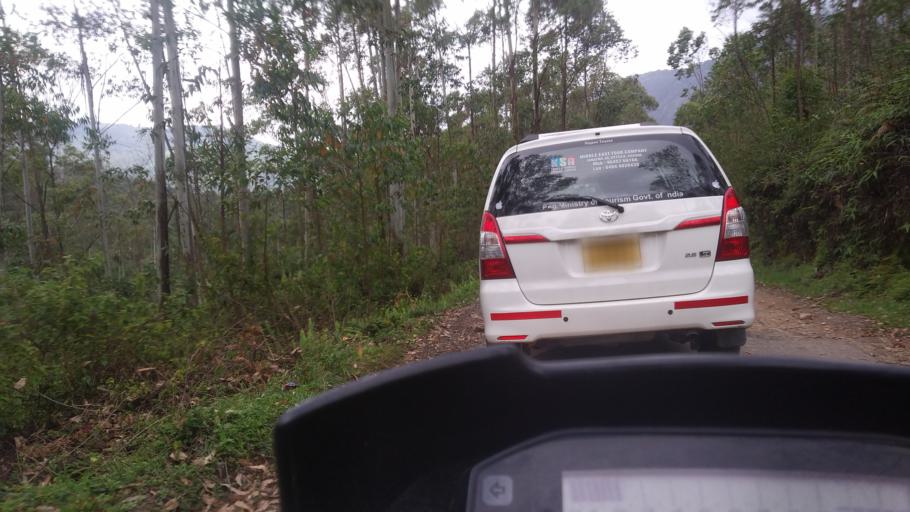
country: IN
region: Kerala
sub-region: Idukki
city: Munnar
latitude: 10.0589
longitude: 77.1079
